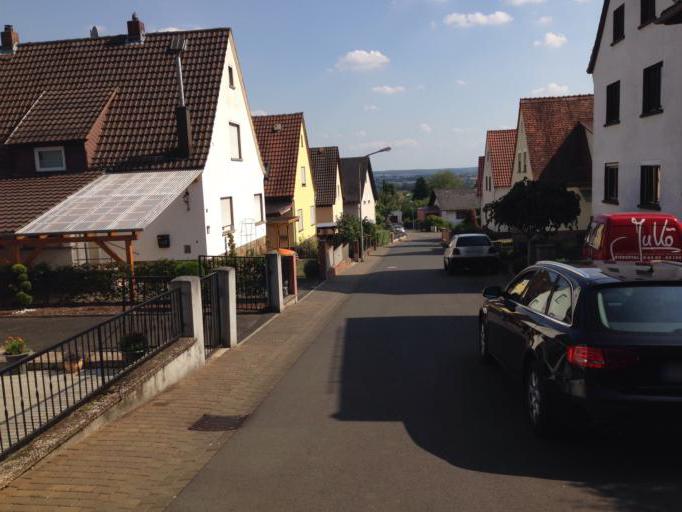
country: DE
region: Hesse
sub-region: Regierungsbezirk Giessen
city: Giessen
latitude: 50.6243
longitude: 8.6562
